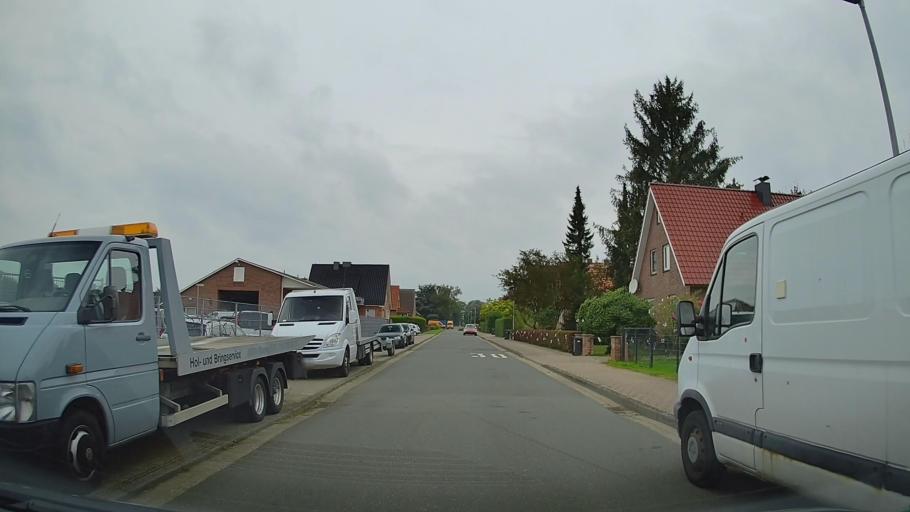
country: DE
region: Lower Saxony
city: Stade
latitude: 53.6702
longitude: 9.4838
